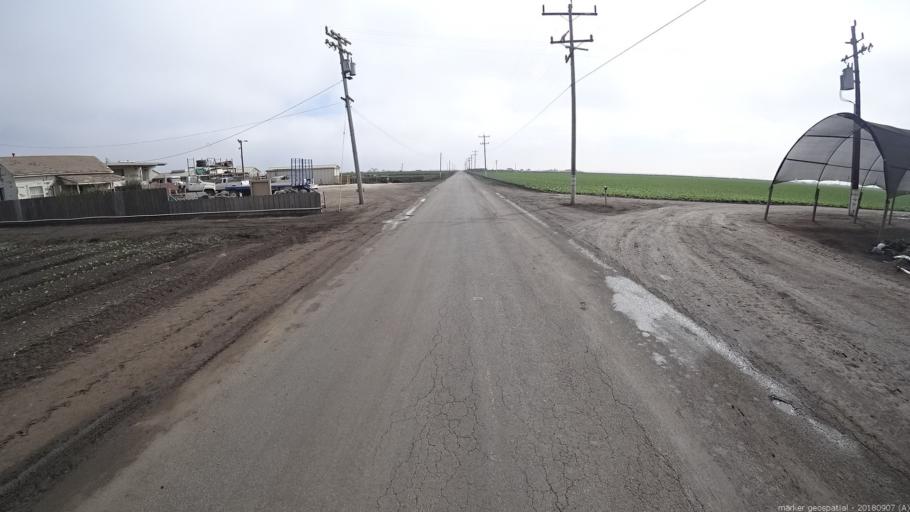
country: US
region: California
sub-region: Monterey County
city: Boronda
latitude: 36.6933
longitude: -121.7204
